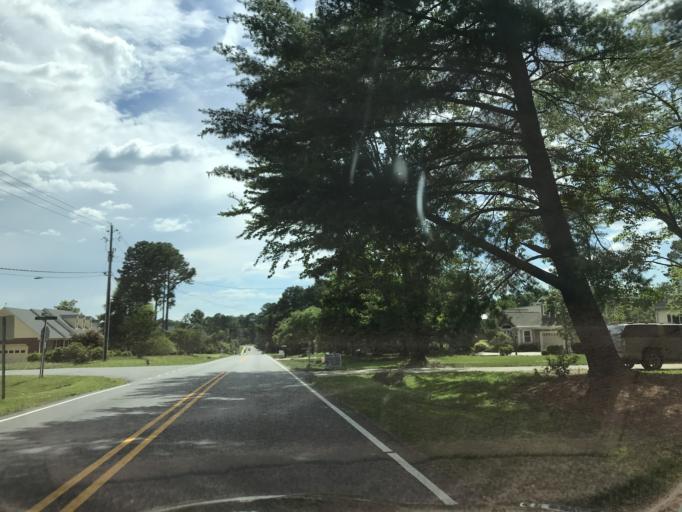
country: US
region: North Carolina
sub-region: Wake County
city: West Raleigh
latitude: 35.8885
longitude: -78.6862
